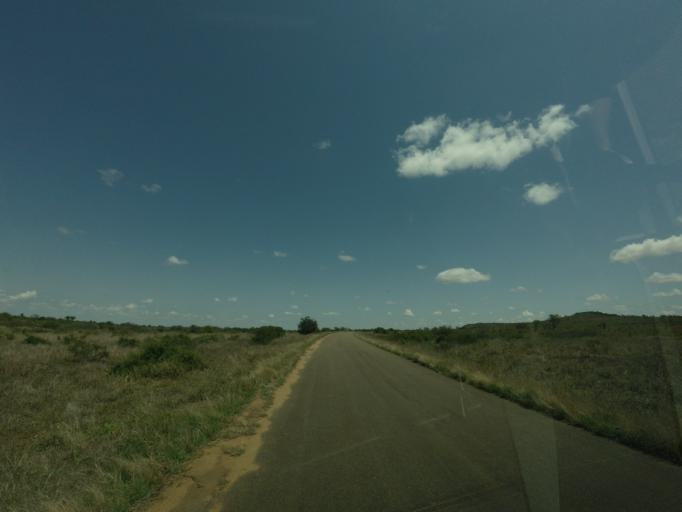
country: ZA
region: Mpumalanga
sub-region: Ehlanzeni District
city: Komatipoort
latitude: -24.8877
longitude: 31.9040
